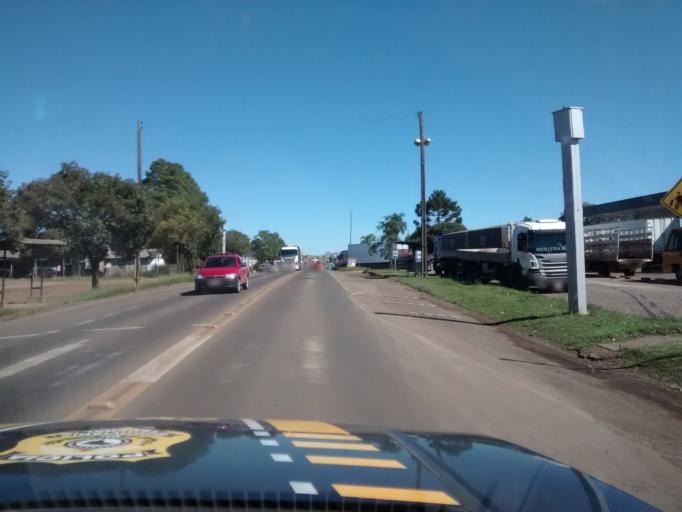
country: BR
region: Rio Grande do Sul
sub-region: Vacaria
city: Vacaria
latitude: -28.5043
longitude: -50.9240
